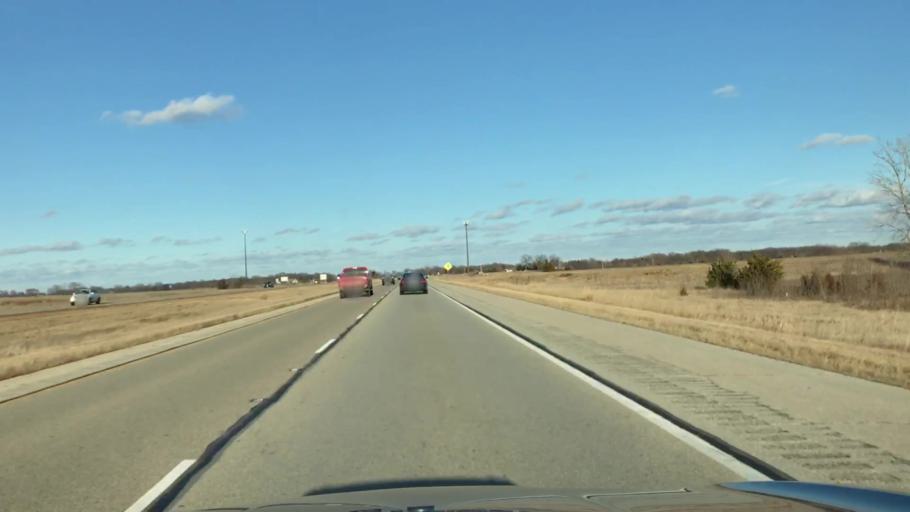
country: US
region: Illinois
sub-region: McLean County
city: Hudson
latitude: 40.5722
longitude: -88.9003
